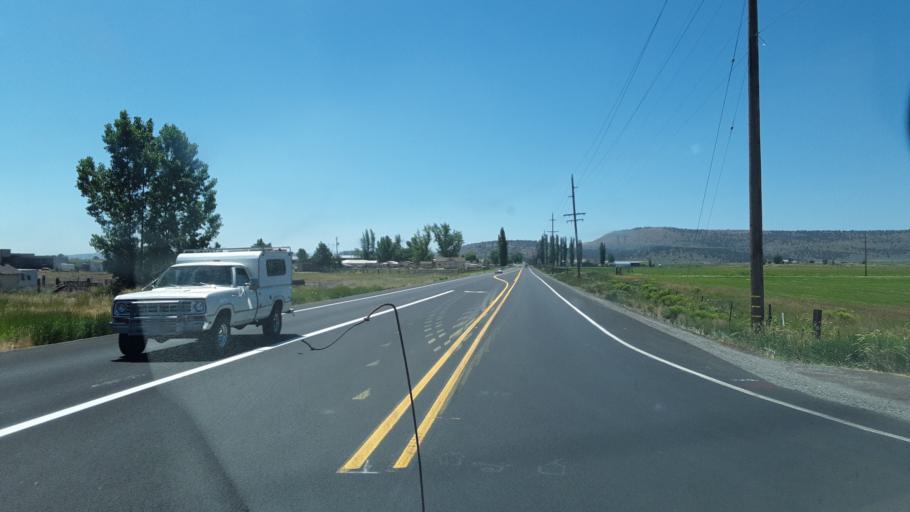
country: US
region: Oregon
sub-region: Klamath County
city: Altamont
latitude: 42.1117
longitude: -121.6986
